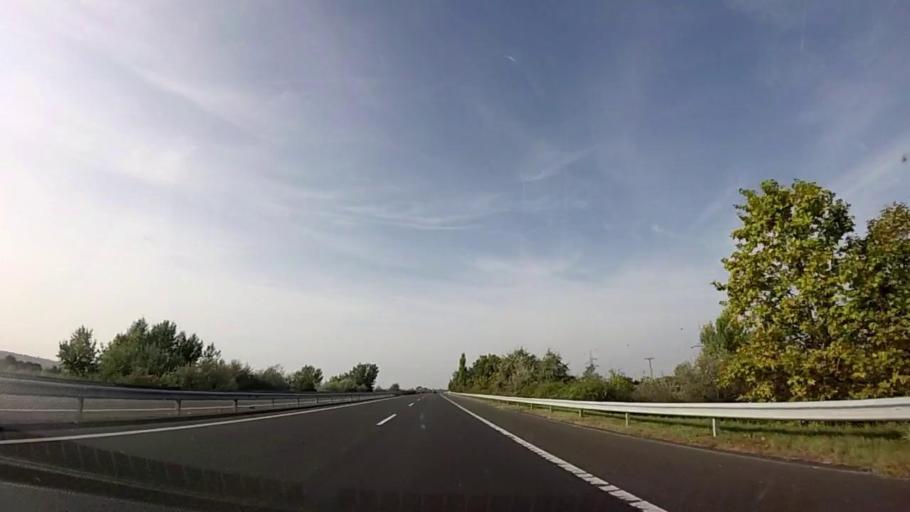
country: HU
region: Somogy
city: Siofok
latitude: 46.9055
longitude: 18.0835
